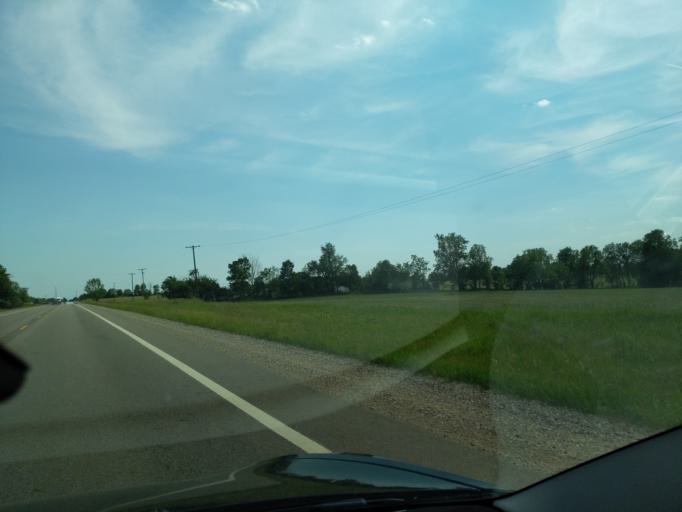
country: US
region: Michigan
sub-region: Barry County
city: Nashville
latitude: 42.6339
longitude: -85.0949
